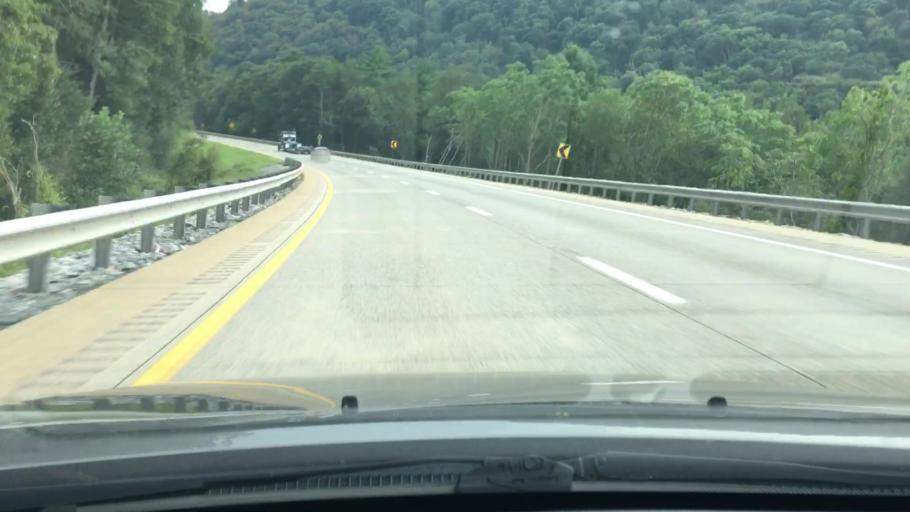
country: US
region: Pennsylvania
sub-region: Lebanon County
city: Jonestown
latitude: 40.4818
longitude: -76.5315
